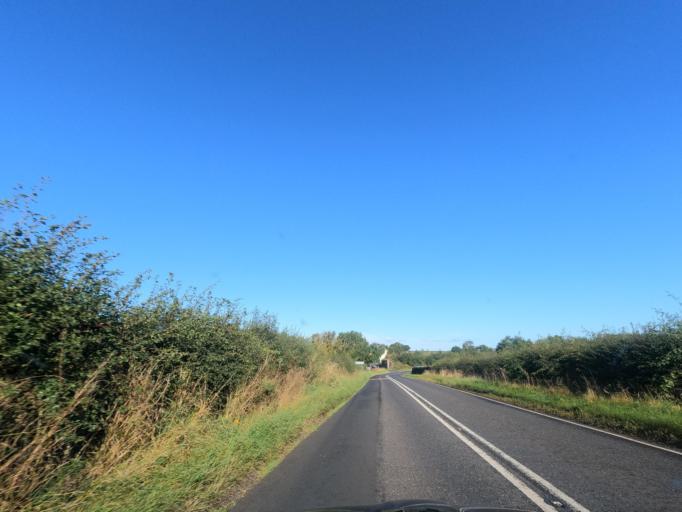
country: GB
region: England
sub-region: Northumberland
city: Ford
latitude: 55.7320
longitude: -2.0940
